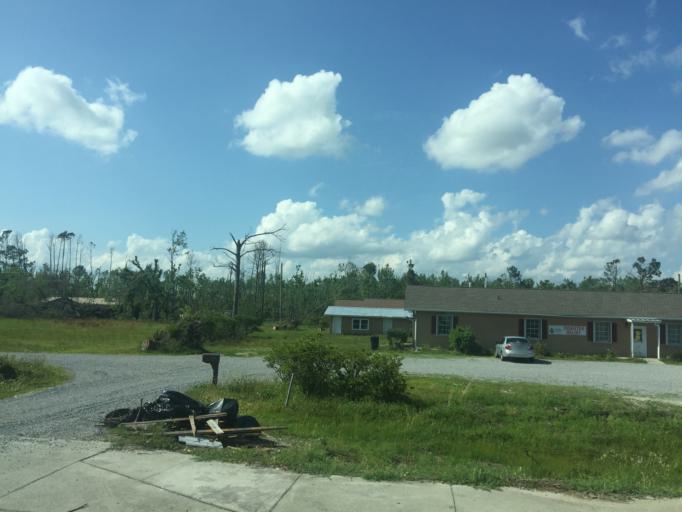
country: US
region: Florida
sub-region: Bay County
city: Cedar Grove
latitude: 30.1676
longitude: -85.6189
